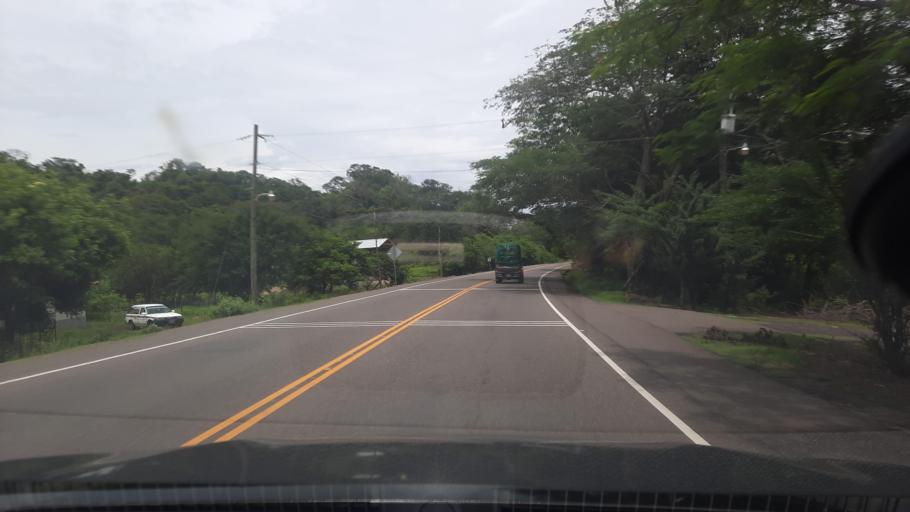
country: HN
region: Valle
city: Goascoran
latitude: 13.5609
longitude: -87.6606
